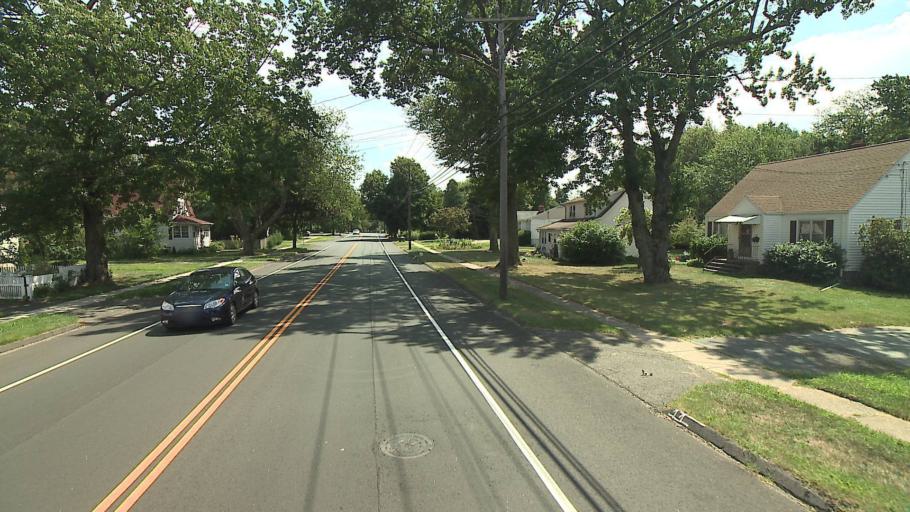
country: US
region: Connecticut
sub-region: Fairfield County
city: Stratford
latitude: 41.2163
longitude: -73.1466
